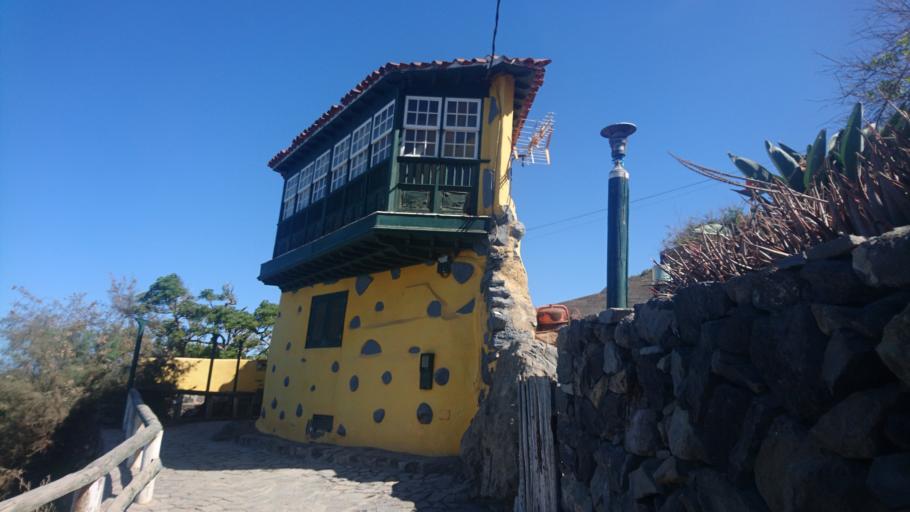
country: ES
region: Canary Islands
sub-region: Provincia de Santa Cruz de Tenerife
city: San Juan de la Rambla
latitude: 28.3950
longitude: -16.6330
